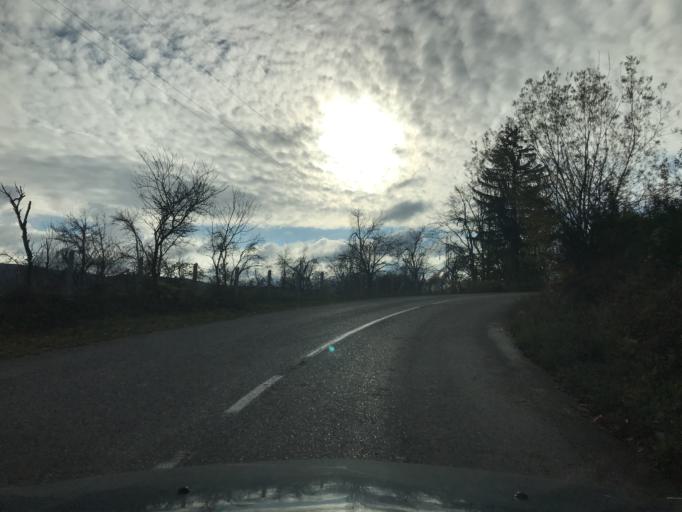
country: BA
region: Republika Srpska
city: Zivinice
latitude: 44.5213
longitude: 17.3614
